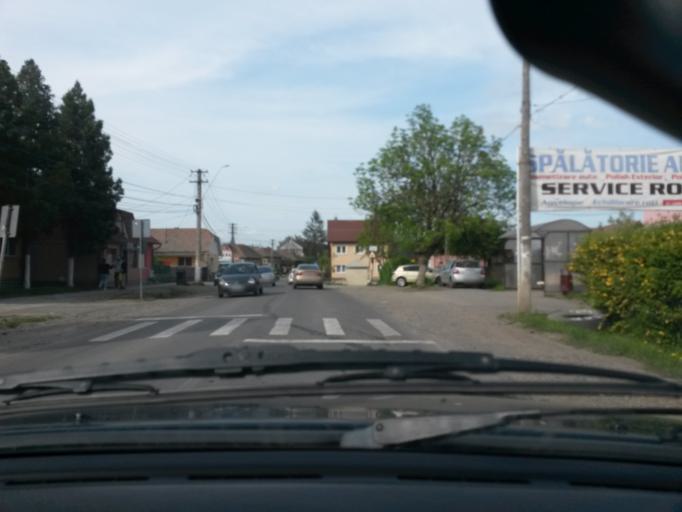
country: RO
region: Mures
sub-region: Comuna Sancraiu de Mures
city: Sancraiu de Mures
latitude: 46.5468
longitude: 24.5188
